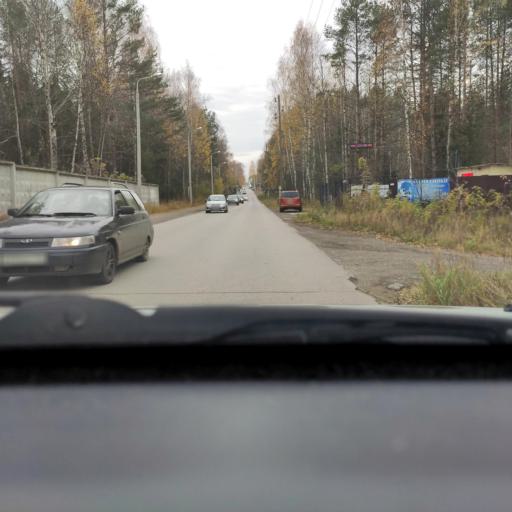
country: RU
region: Perm
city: Kondratovo
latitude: 58.0625
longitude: 56.1251
